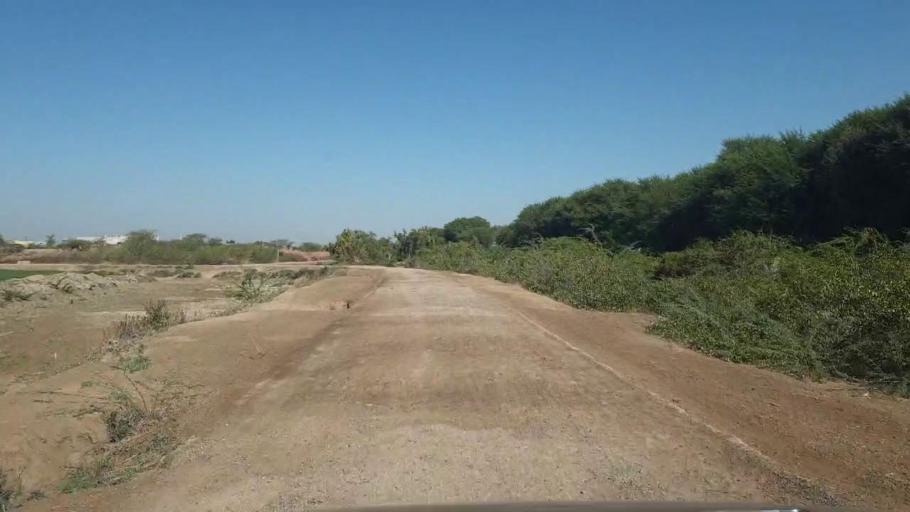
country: PK
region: Sindh
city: Umarkot
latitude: 25.3871
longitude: 69.6738
